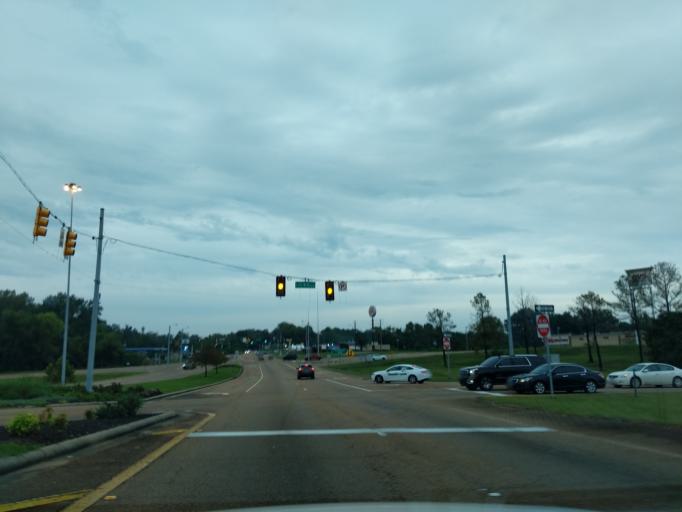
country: US
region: Mississippi
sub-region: Warren County
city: Vicksburg
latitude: 32.3203
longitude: -90.8772
